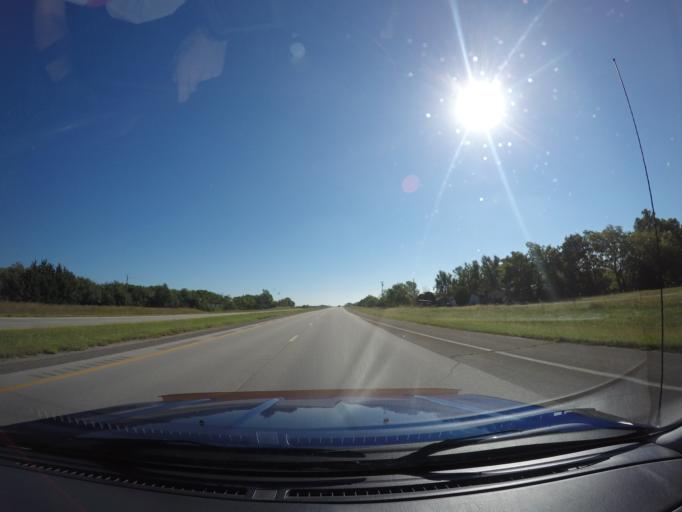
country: US
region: Kansas
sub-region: Pottawatomie County
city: Wamego
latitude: 39.2091
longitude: -96.4120
